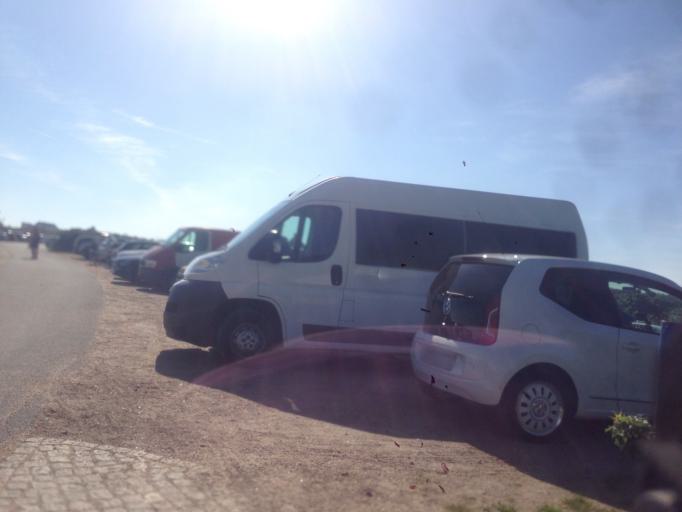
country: DE
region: Schleswig-Holstein
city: Westerland
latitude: 54.9632
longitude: 8.3346
